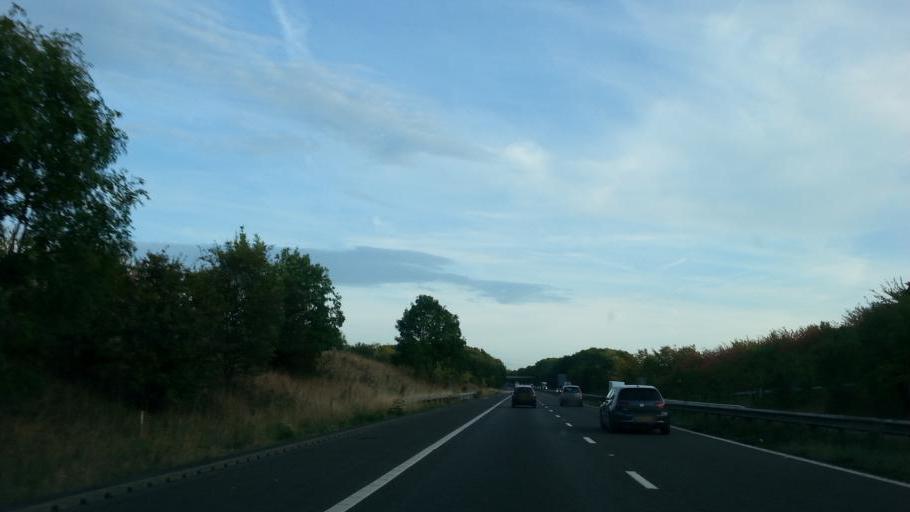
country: GB
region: England
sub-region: Doncaster
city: Doncaster
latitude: 53.4780
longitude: -1.1468
